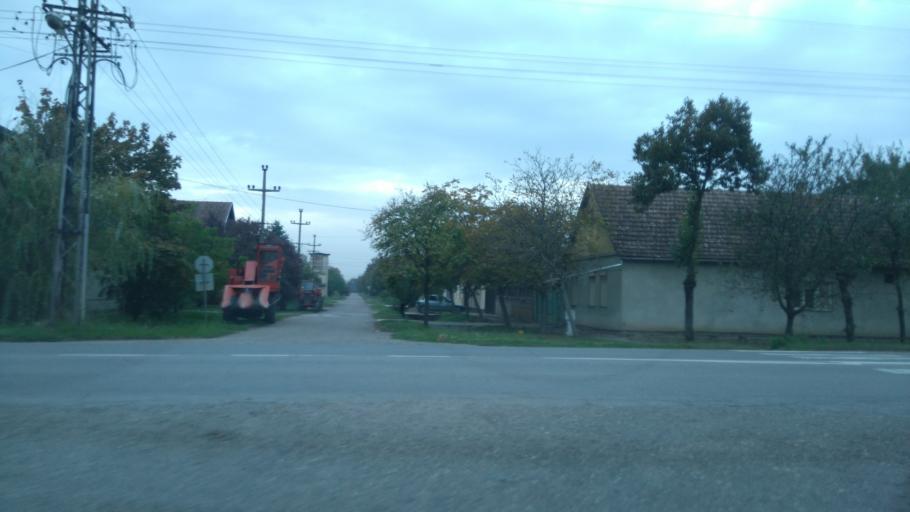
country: RS
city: Mol
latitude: 45.7705
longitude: 20.1288
